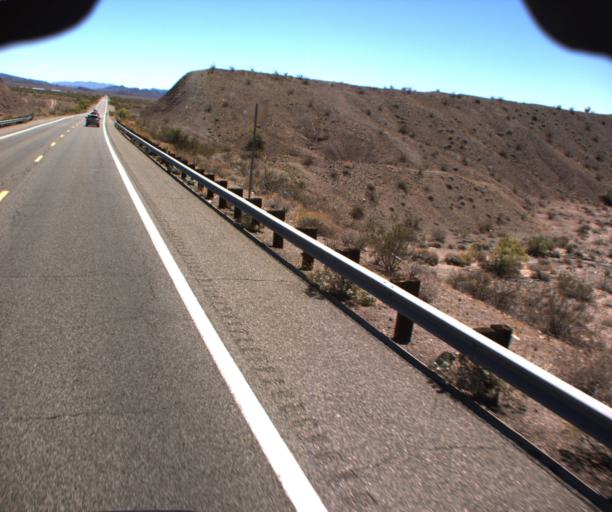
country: US
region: Arizona
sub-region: Mohave County
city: Lake Havasu City
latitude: 34.4262
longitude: -114.2075
